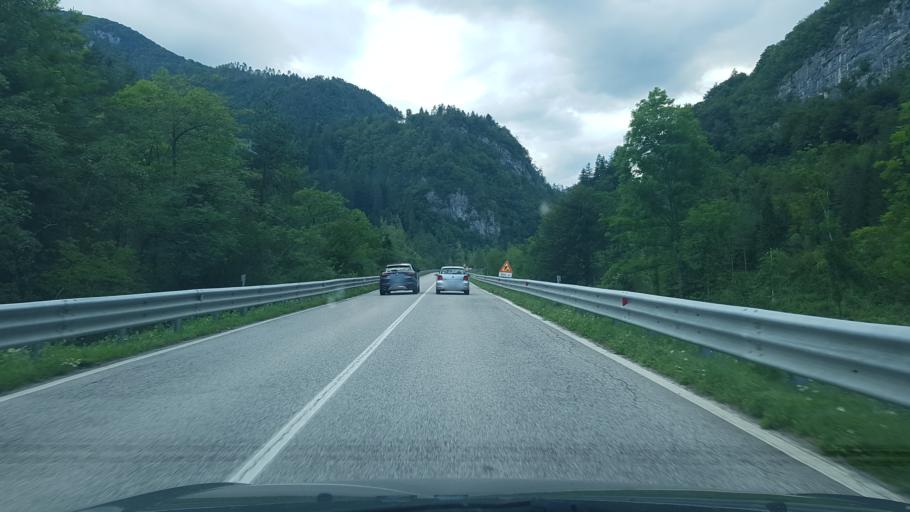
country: IT
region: Friuli Venezia Giulia
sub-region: Provincia di Udine
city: Raveo
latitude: 46.4552
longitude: 12.8746
